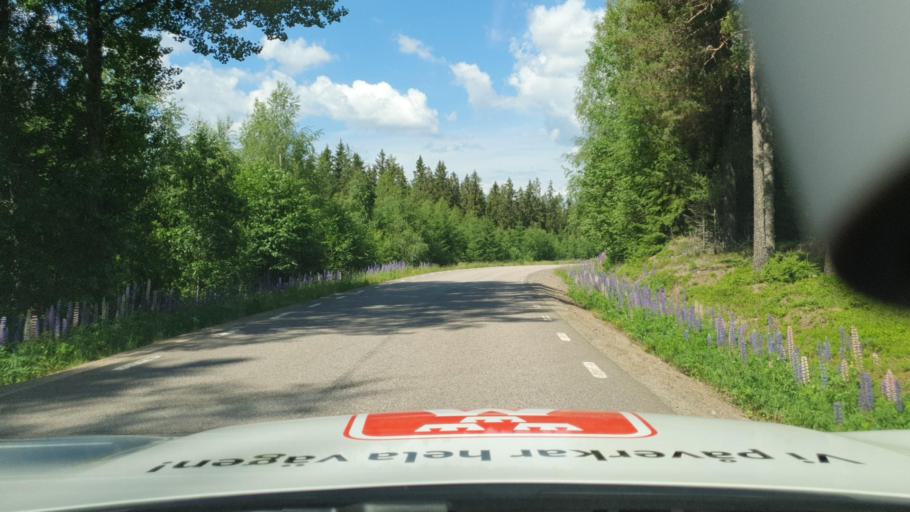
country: SE
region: Vaermland
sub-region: Torsby Kommun
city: Torsby
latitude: 60.4289
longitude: 12.9016
